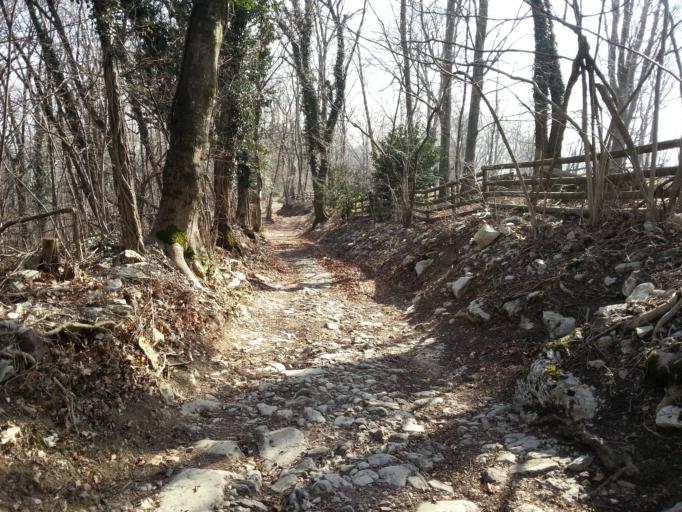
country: IT
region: Lombardy
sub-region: Provincia di Como
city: Albavilla
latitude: 45.8204
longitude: 9.1759
